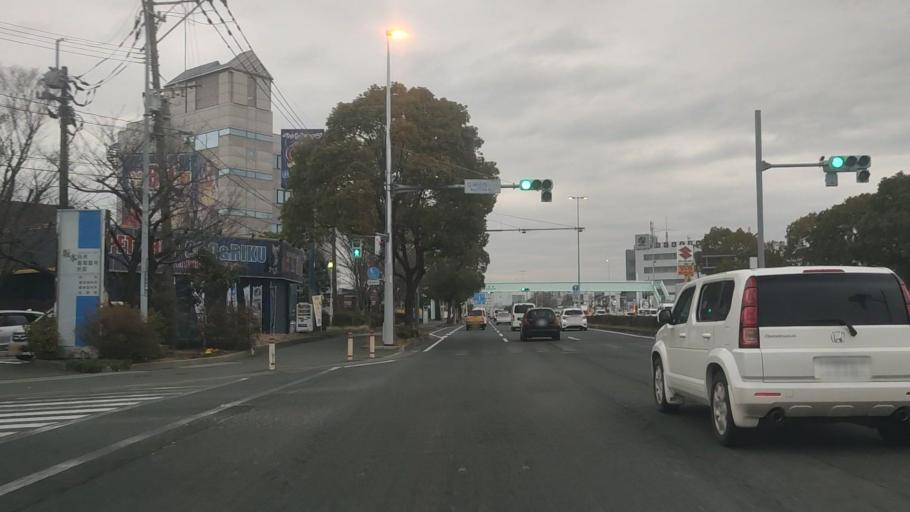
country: JP
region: Kumamoto
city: Kumamoto
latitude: 32.7740
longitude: 130.7348
